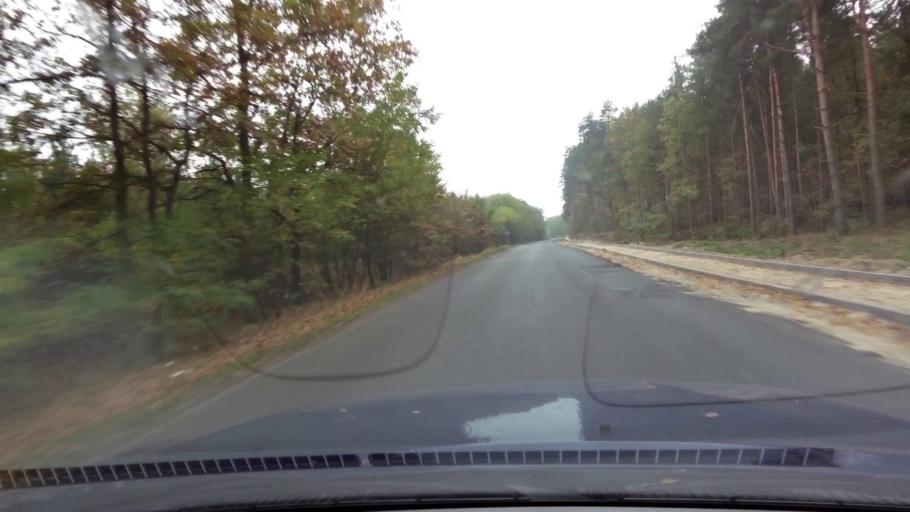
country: PL
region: West Pomeranian Voivodeship
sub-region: Powiat goleniowski
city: Goleniow
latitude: 53.5131
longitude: 14.7438
